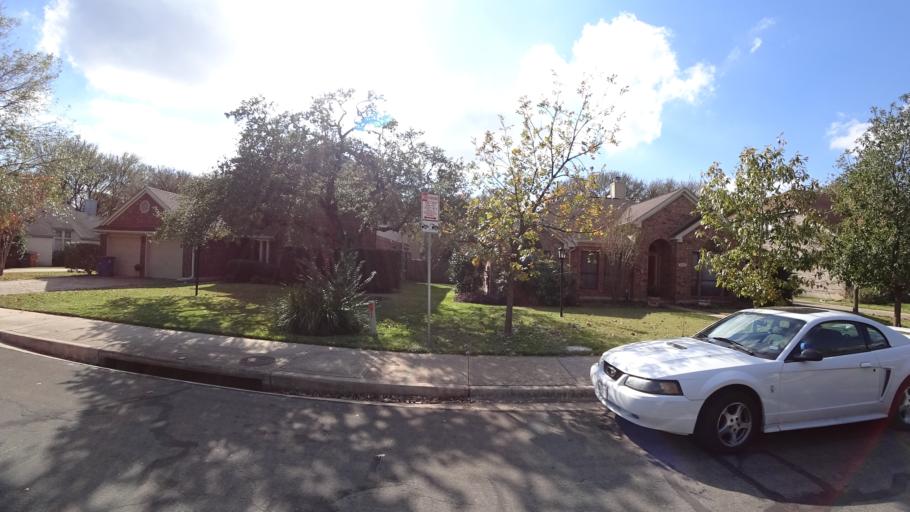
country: US
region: Texas
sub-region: Travis County
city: Shady Hollow
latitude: 30.1811
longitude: -97.8555
